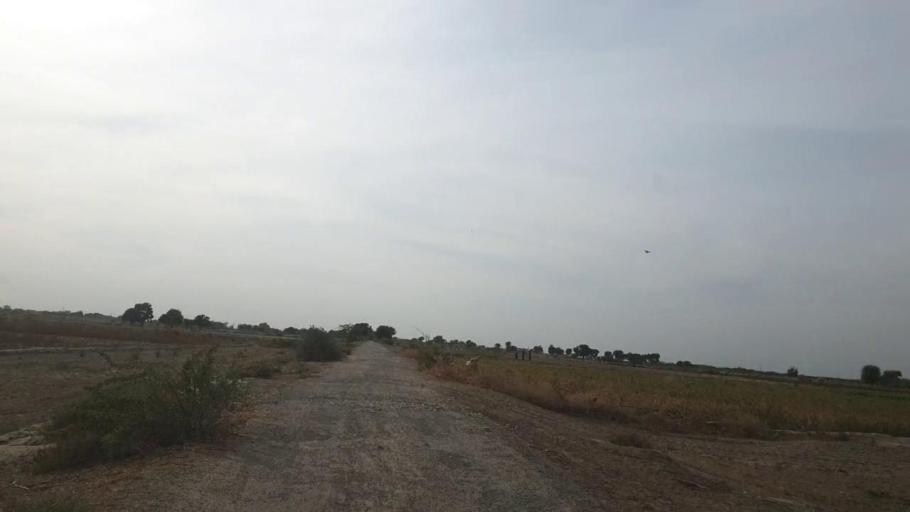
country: PK
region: Sindh
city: Nabisar
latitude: 25.0003
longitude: 69.5355
